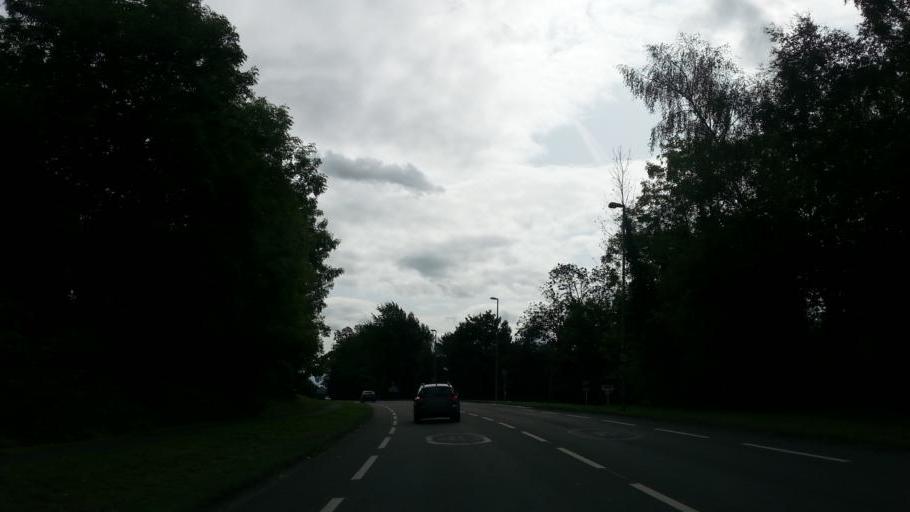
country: GB
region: England
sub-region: Leicestershire
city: Market Harborough
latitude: 52.4879
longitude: -0.9341
